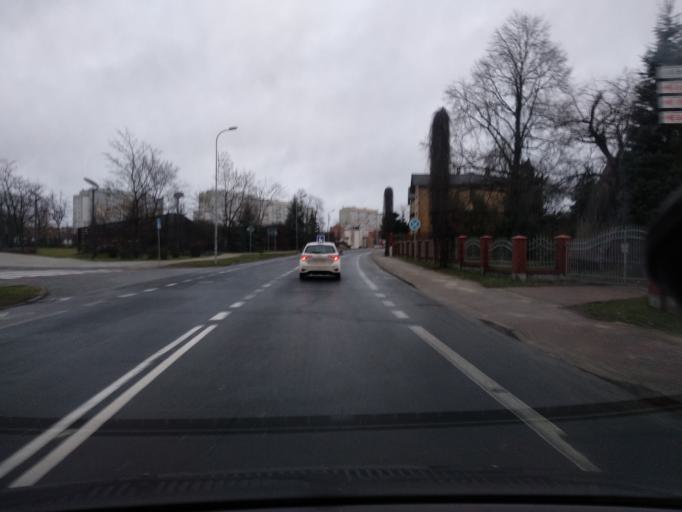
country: PL
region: Lower Silesian Voivodeship
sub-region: Powiat polkowicki
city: Polkowice
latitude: 51.5021
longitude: 16.0696
